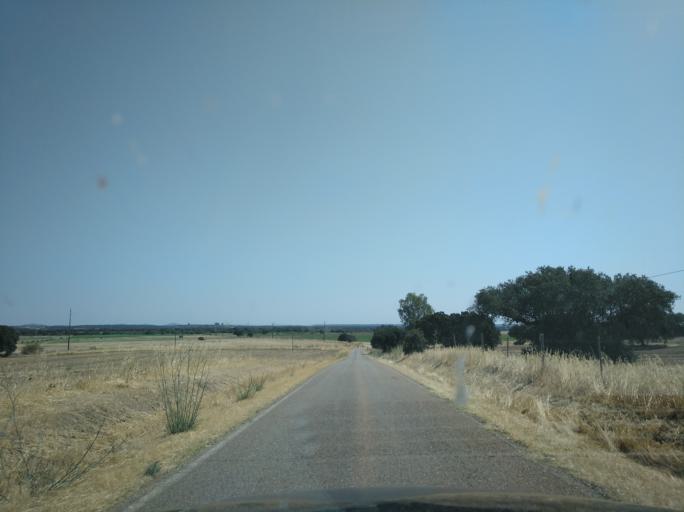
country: PT
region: Portalegre
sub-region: Campo Maior
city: Campo Maior
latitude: 39.0349
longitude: -6.9889
